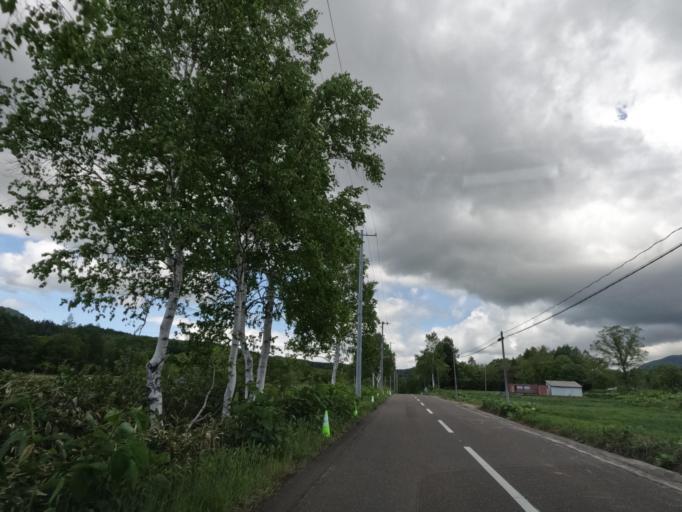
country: JP
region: Hokkaido
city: Tobetsu
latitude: 43.4539
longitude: 141.5909
